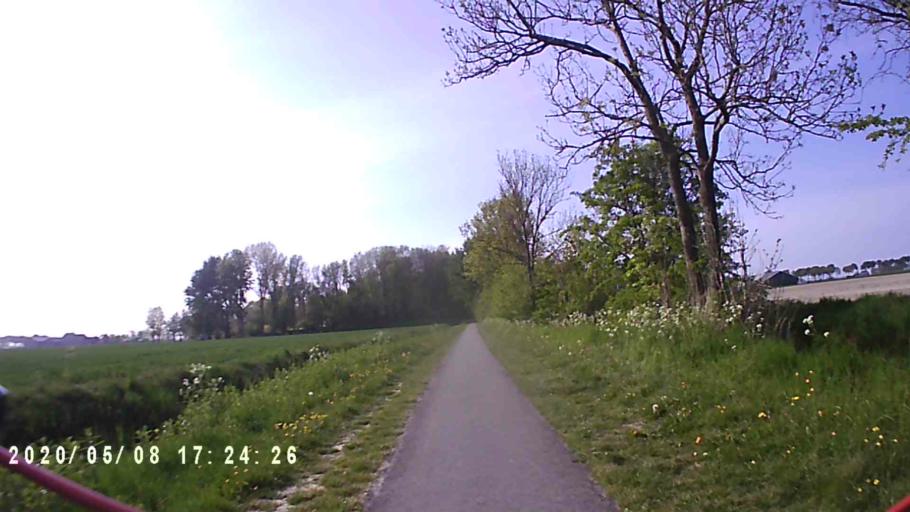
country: NL
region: Groningen
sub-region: Gemeente Winsum
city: Winsum
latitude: 53.3828
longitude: 6.5445
